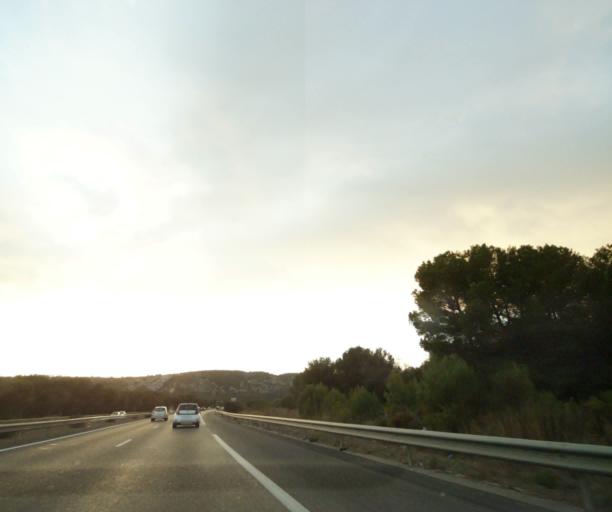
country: FR
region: Provence-Alpes-Cote d'Azur
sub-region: Departement des Bouches-du-Rhone
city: Ensues-la-Redonne
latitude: 43.3737
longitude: 5.1946
